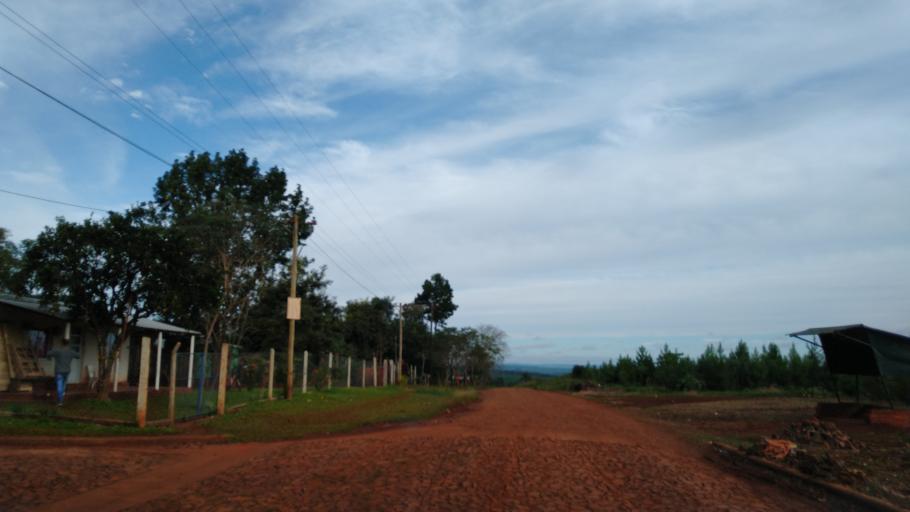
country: AR
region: Misiones
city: Capiovi
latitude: -26.9442
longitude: -55.0964
